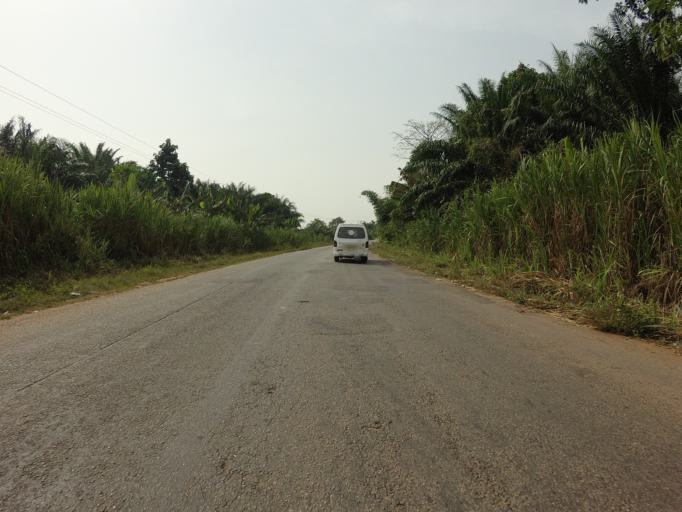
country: GH
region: Volta
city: Ho
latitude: 6.3745
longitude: 0.1887
